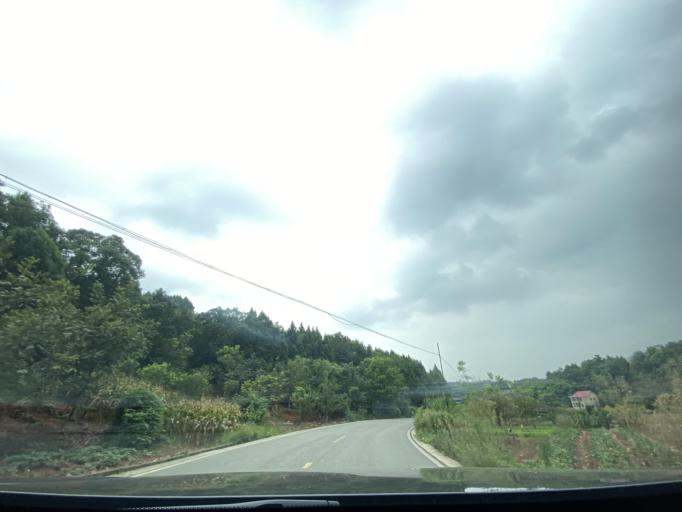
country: CN
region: Sichuan
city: Jiancheng
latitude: 30.5366
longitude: 104.5286
